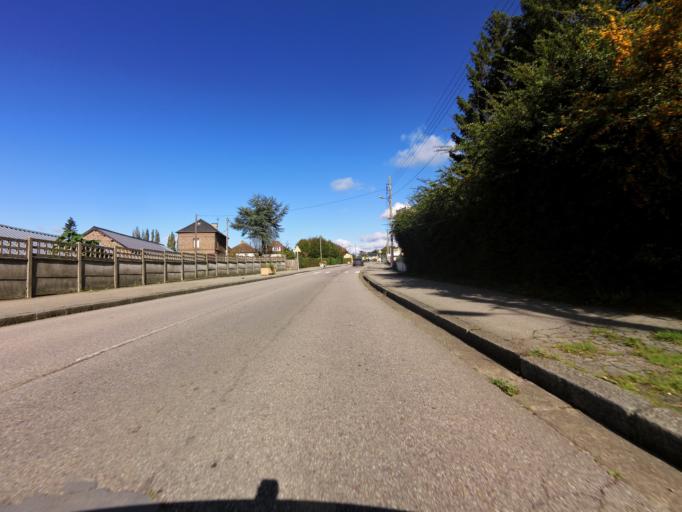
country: FR
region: Lower Normandy
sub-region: Departement de l'Orne
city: Vimoutiers
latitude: 48.9326
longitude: 0.2006
